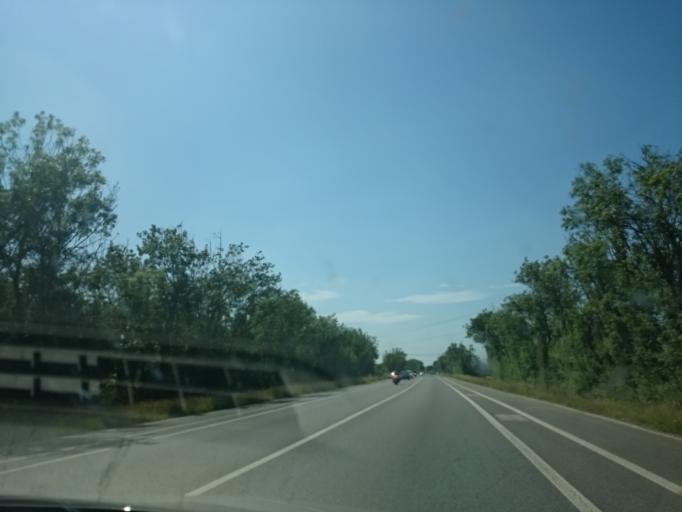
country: FR
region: Pays de la Loire
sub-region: Departement de la Loire-Atlantique
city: Indre
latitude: 47.2055
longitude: -1.6783
